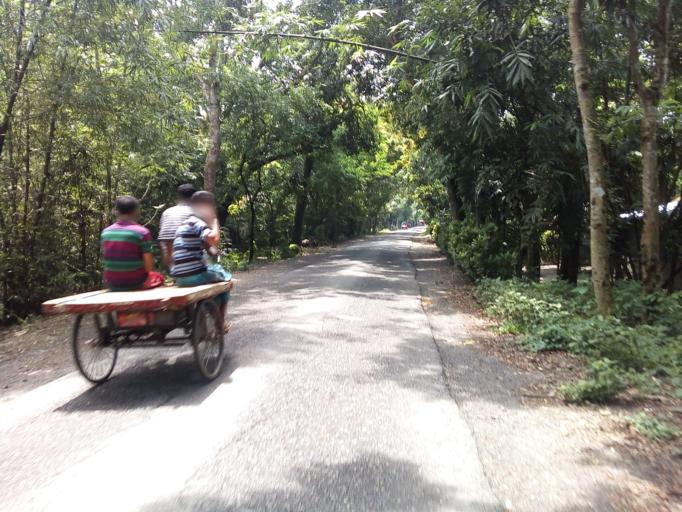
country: BD
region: Dhaka
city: Faridpur
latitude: 23.5609
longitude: 89.6276
